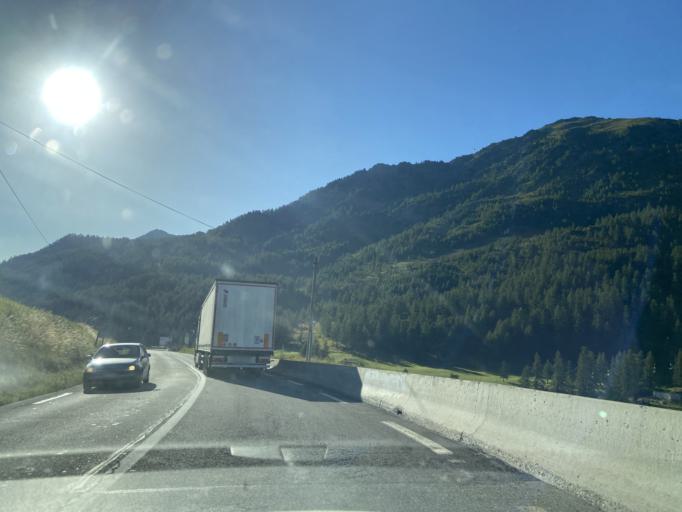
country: IT
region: Piedmont
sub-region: Provincia di Torino
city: Claviere
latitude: 44.9332
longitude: 6.7346
